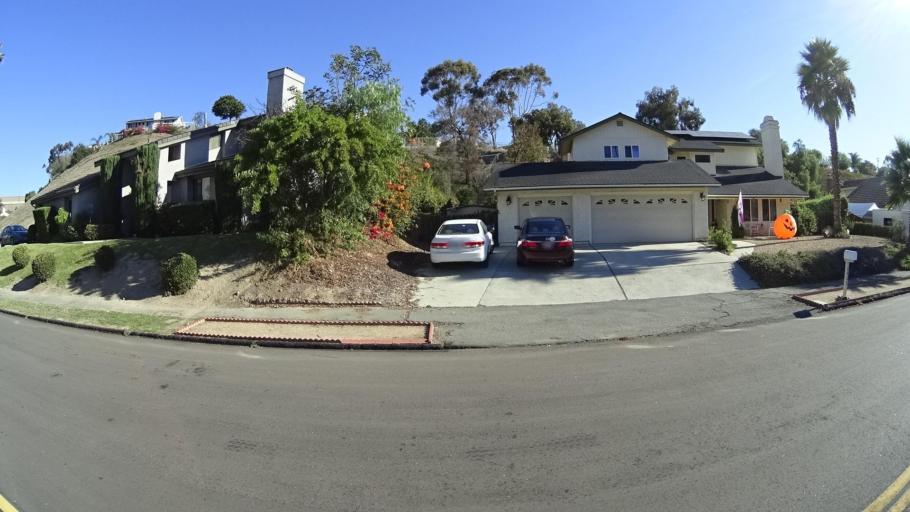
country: US
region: California
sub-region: San Diego County
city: Bonita
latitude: 32.6846
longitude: -117.0202
